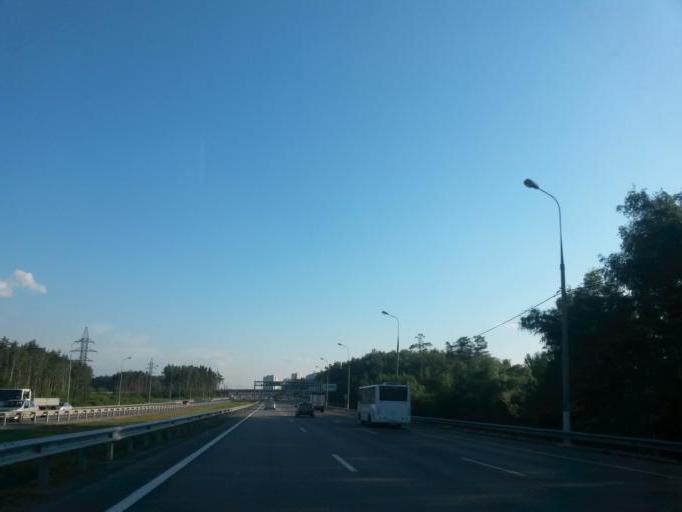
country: RU
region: Moskovskaya
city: Vostryakovo
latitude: 55.4099
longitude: 37.7900
